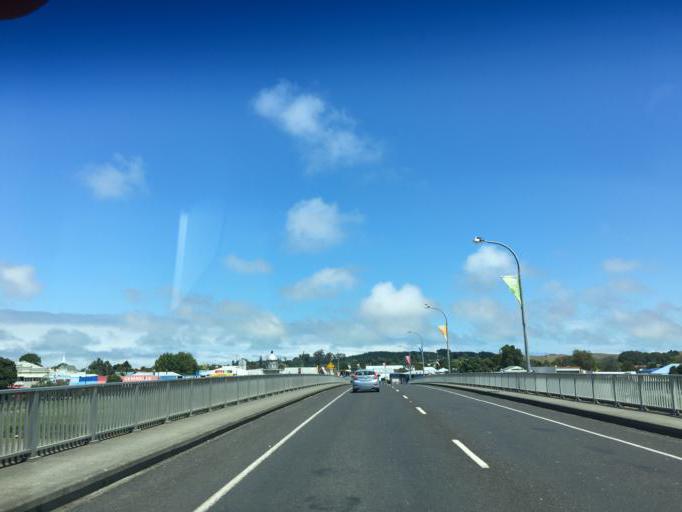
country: NZ
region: Hawke's Bay
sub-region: Wairoa District
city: Wairoa
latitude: -39.0314
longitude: 177.4188
